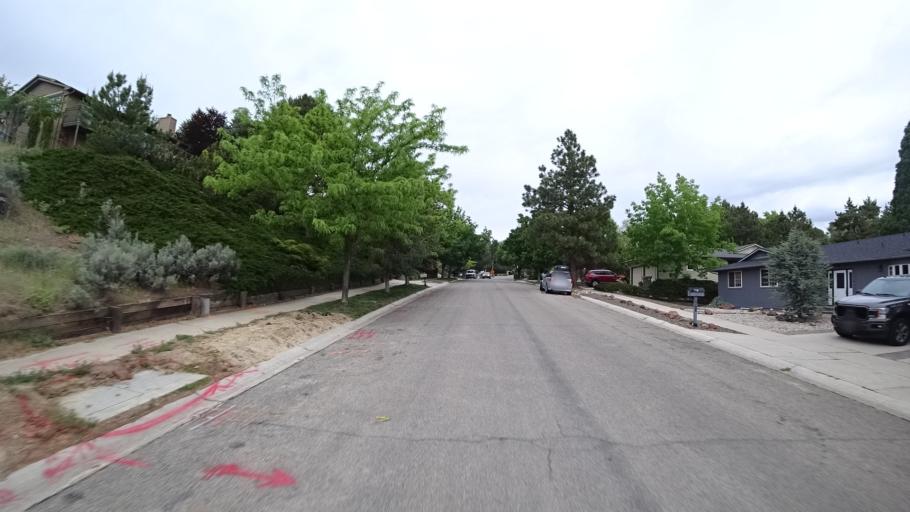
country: US
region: Idaho
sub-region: Ada County
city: Boise
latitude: 43.6141
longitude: -116.1708
